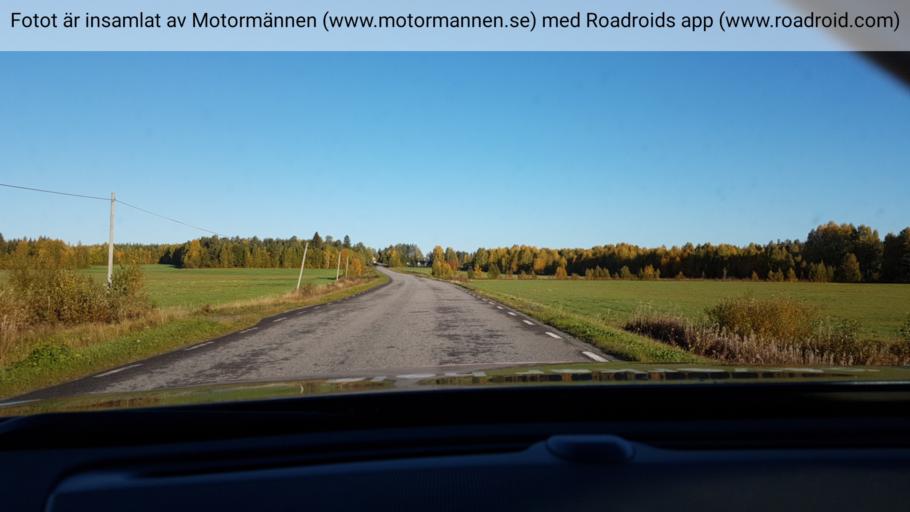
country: SE
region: Norrbotten
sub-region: Bodens Kommun
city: Boden
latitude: 65.8963
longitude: 21.6760
